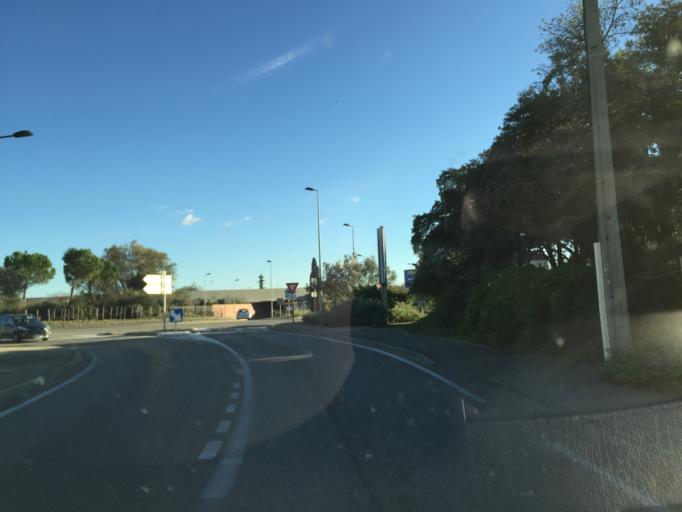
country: FR
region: Provence-Alpes-Cote d'Azur
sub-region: Departement du Vaucluse
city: Sorgues
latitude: 44.0187
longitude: 4.8682
